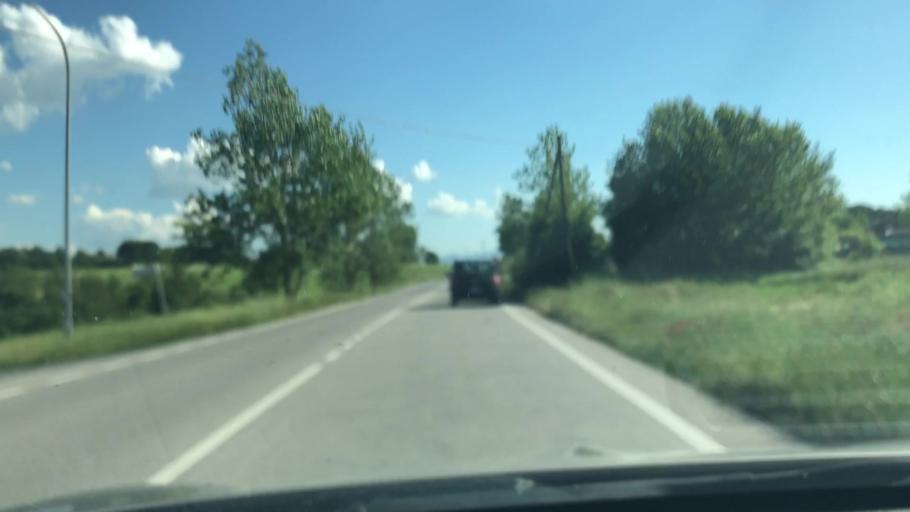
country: IT
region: Tuscany
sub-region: Province of Pisa
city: Il Romito
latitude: 43.6497
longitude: 10.6562
